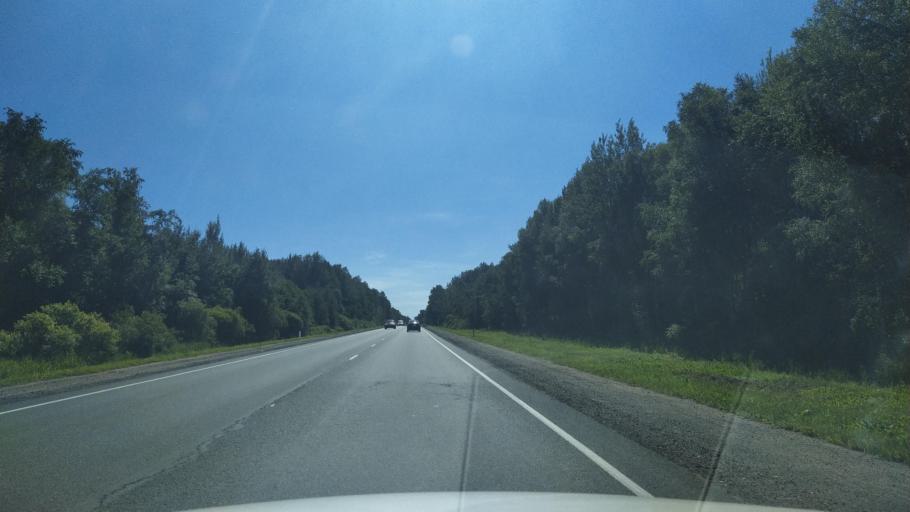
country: RU
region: Pskov
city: Pskov
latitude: 57.7770
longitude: 28.4006
